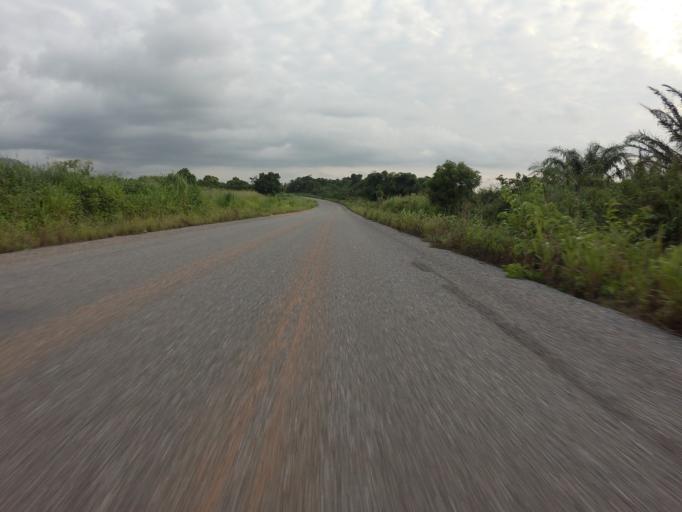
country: GH
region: Volta
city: Kpandu
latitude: 6.8398
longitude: 0.3859
